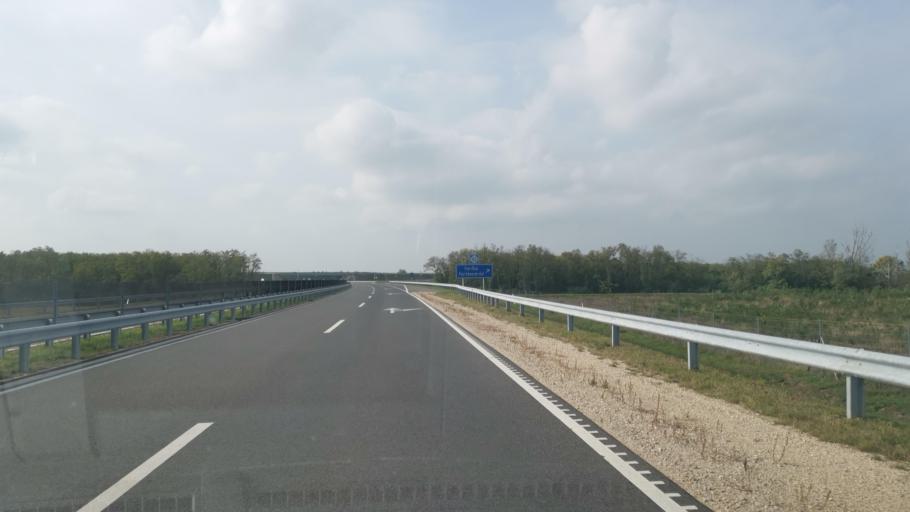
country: HU
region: Gyor-Moson-Sopron
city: Fertoszentmiklos
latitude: 47.5869
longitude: 16.9422
